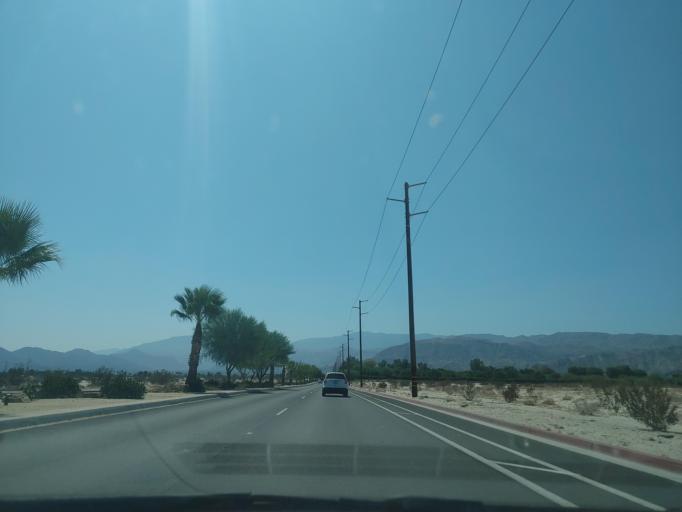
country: US
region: California
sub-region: Riverside County
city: Thousand Palms
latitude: 33.7845
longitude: -116.4060
